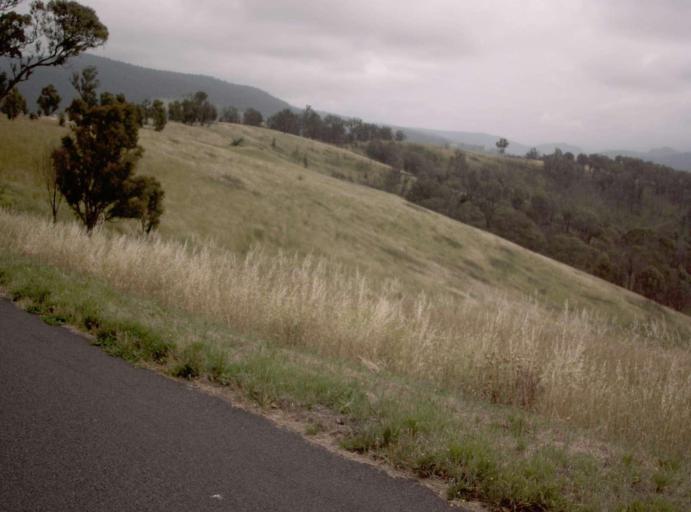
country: AU
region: Victoria
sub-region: Wellington
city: Heyfield
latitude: -37.8347
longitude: 146.6810
